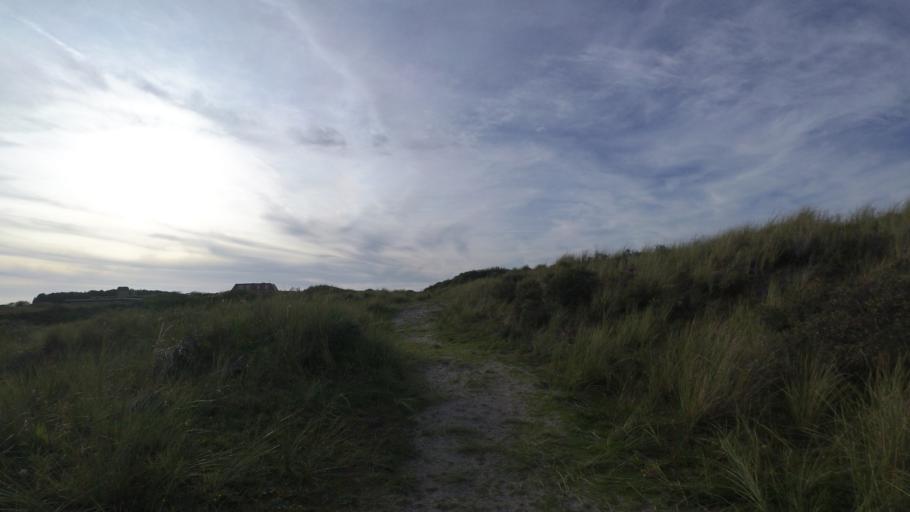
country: NL
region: Friesland
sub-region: Gemeente Ameland
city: Nes
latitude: 53.4601
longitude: 5.8110
